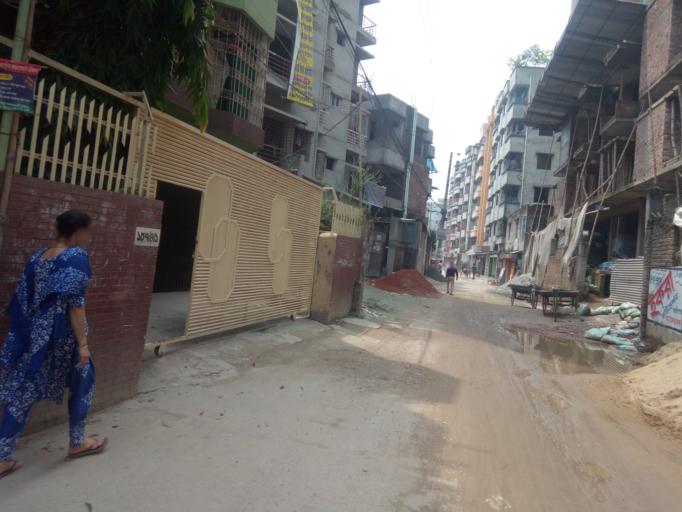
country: BD
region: Dhaka
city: Paltan
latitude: 23.7614
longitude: 90.4272
